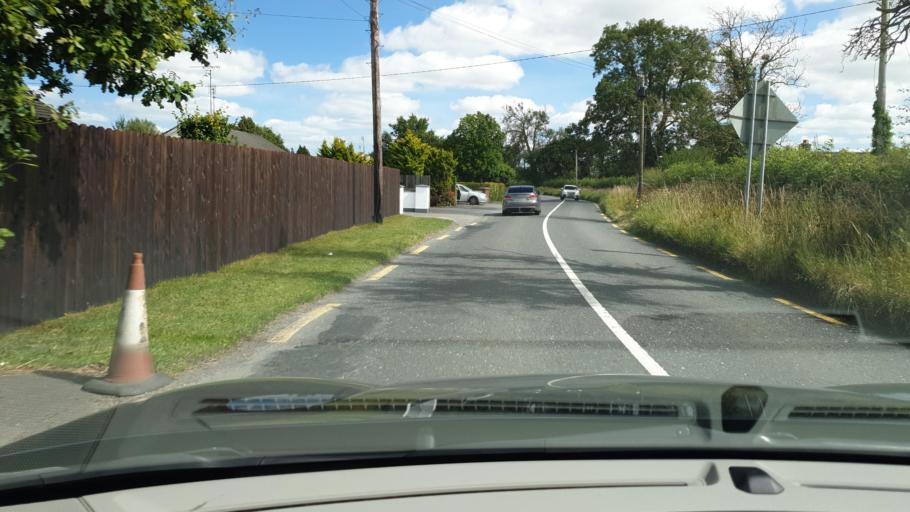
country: IE
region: Leinster
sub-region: Kildare
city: Maynooth
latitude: 53.4402
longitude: -6.5505
